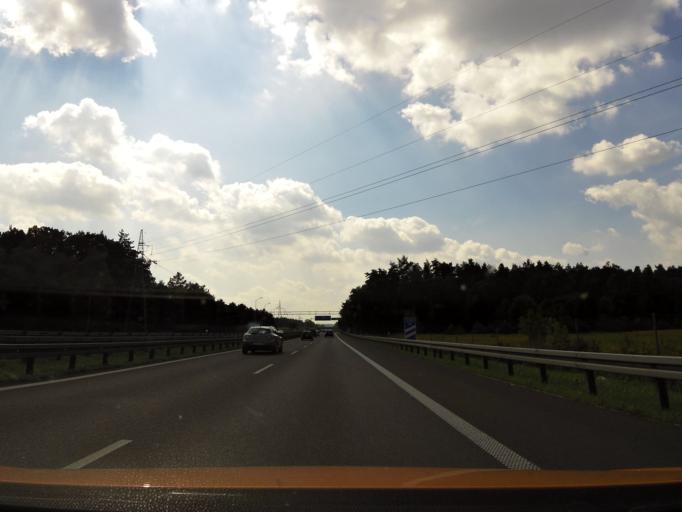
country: PL
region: West Pomeranian Voivodeship
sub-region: Powiat gryfinski
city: Stare Czarnowo
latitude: 53.4005
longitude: 14.7211
